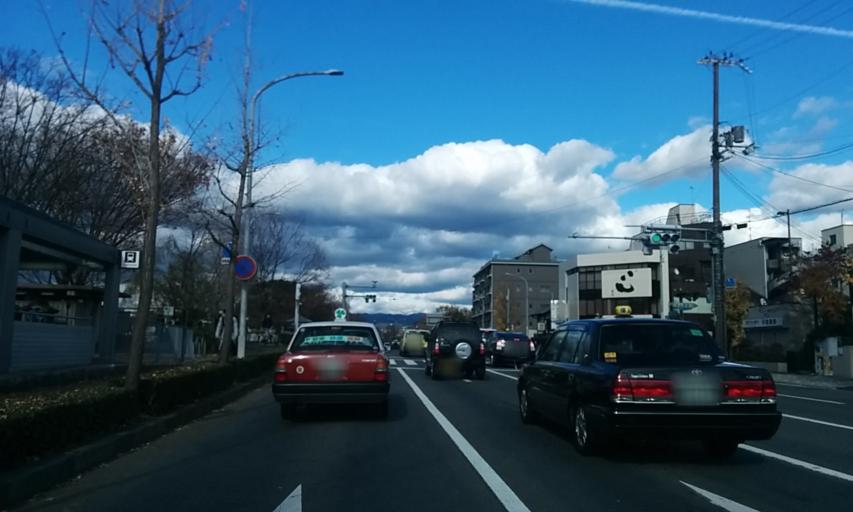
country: JP
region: Kyoto
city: Kyoto
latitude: 35.0171
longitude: 135.7722
